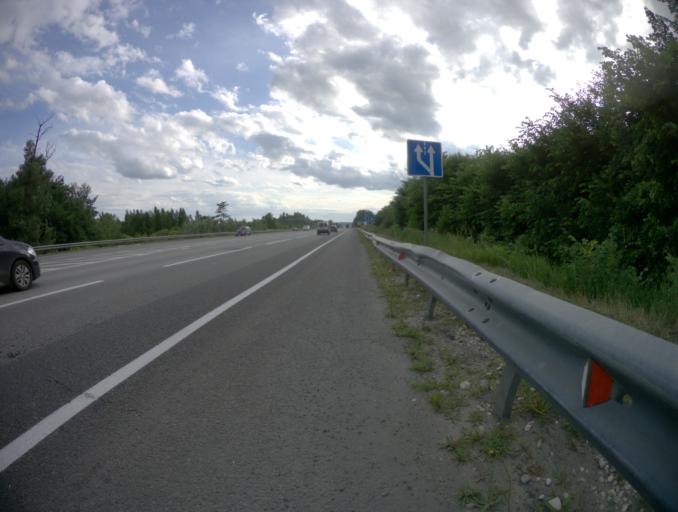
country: RU
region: Vladimir
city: Gorokhovets
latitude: 56.2112
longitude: 42.7436
